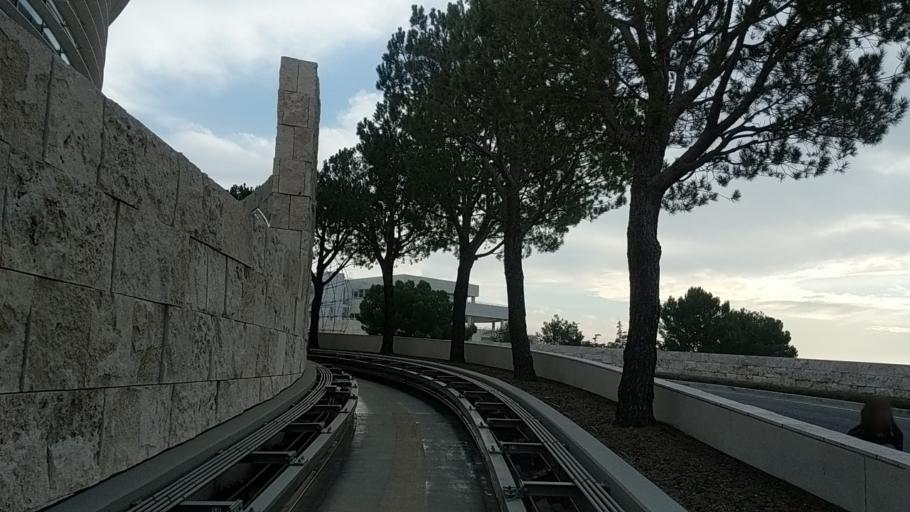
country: US
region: California
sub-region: Los Angeles County
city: Westwood, Los Angeles
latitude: 34.0791
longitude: -118.4754
